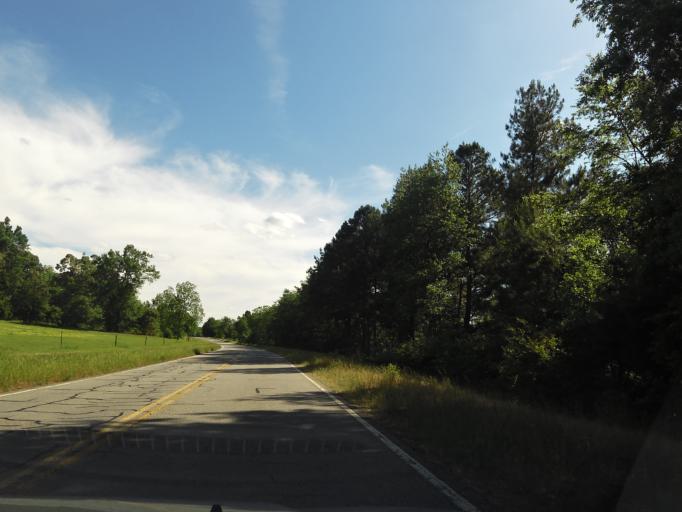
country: US
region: South Carolina
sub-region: Bamberg County
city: Denmark
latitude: 33.2295
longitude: -81.1749
